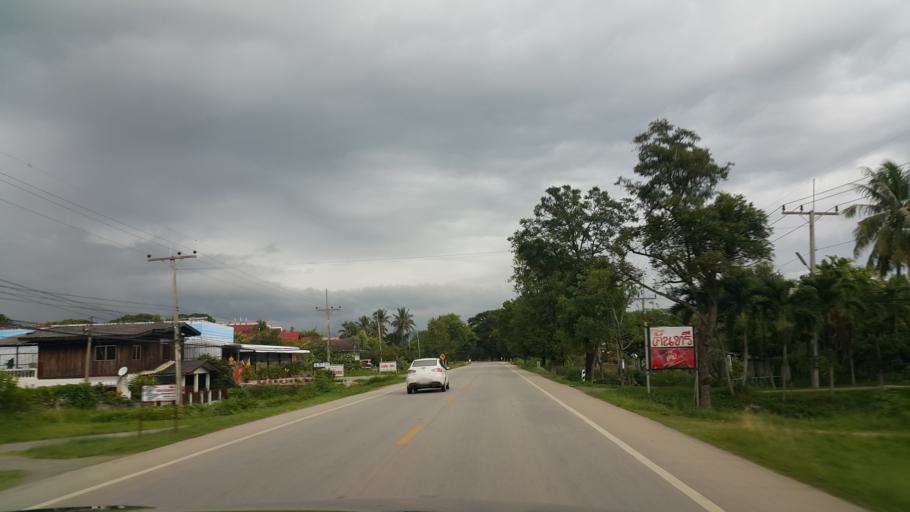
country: TH
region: Phayao
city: Dok Kham Tai
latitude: 19.1989
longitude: 100.0302
